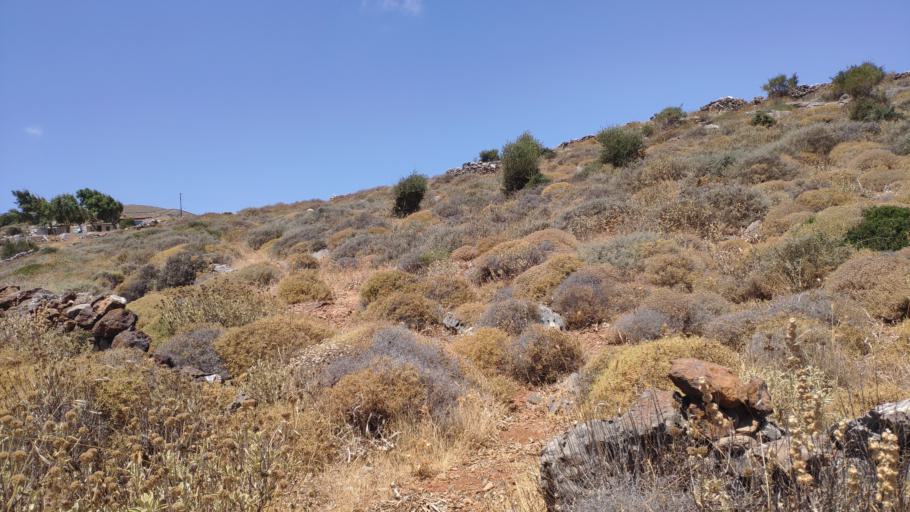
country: GR
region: South Aegean
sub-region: Nomos Kykladon
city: Kythnos
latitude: 37.3799
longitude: 24.4545
